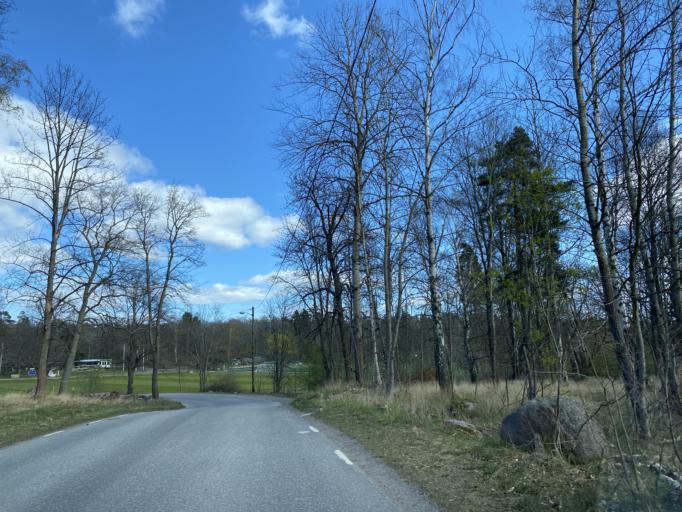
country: SE
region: Stockholm
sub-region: Lidingo
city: Lidingoe
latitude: 59.3338
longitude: 18.1327
